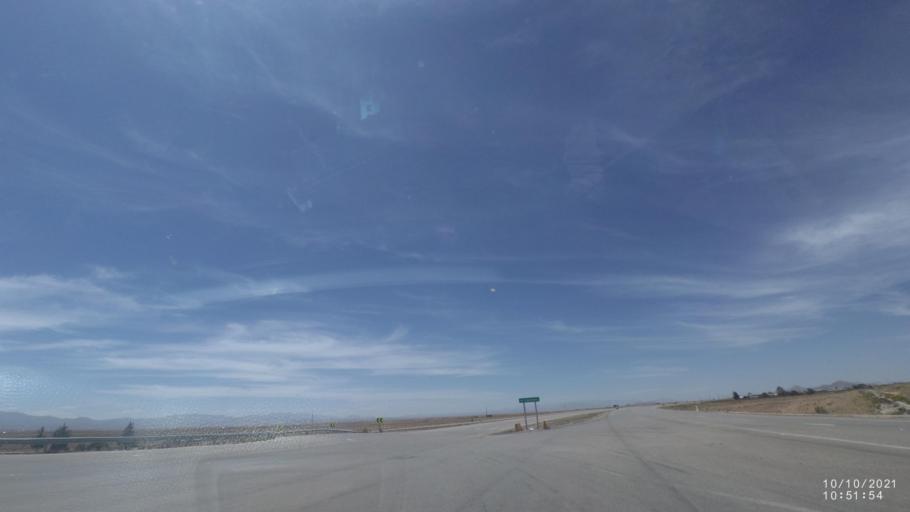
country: BO
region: La Paz
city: Colquiri
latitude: -17.6570
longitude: -67.2080
